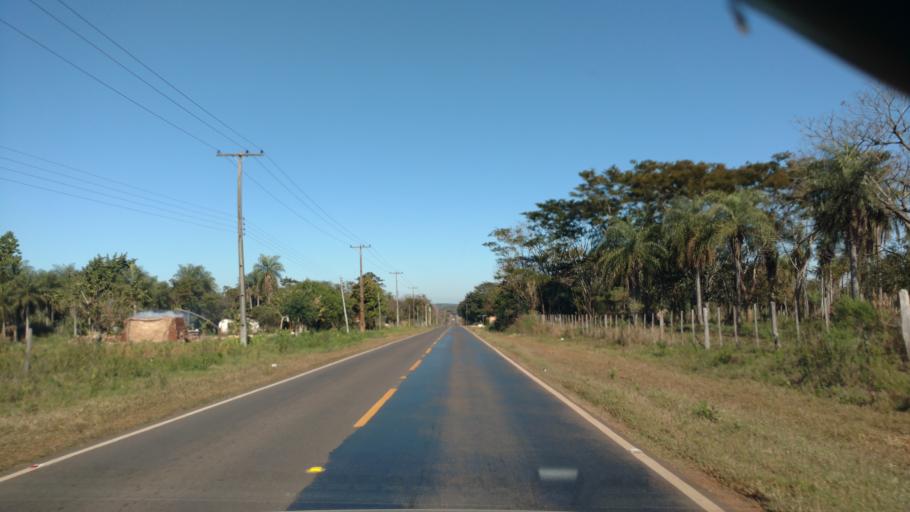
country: PY
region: Paraguari
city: Pirayu
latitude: -25.5163
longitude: -57.2604
